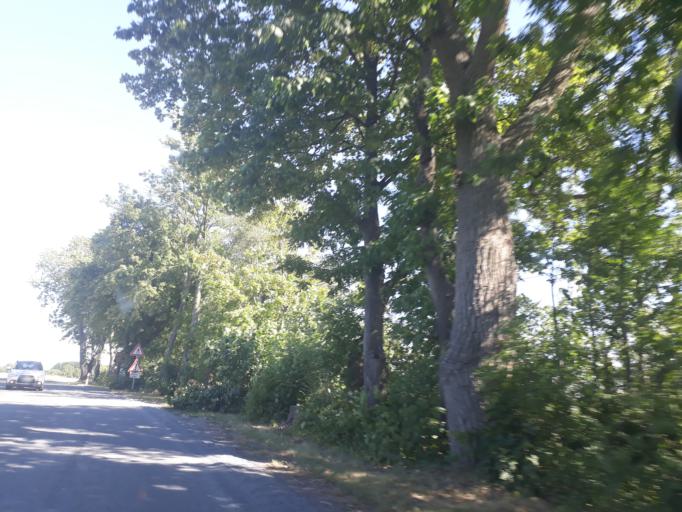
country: DE
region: Saxony
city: Freital
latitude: 51.0240
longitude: 13.6618
